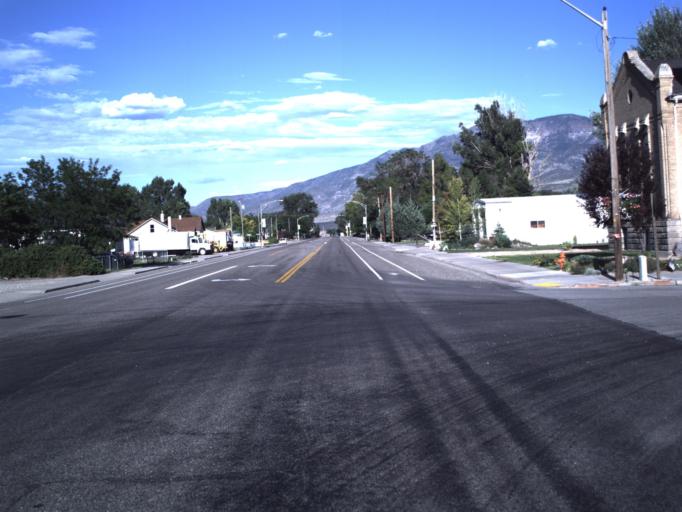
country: US
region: Utah
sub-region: Sevier County
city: Monroe
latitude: 38.6830
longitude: -112.1489
